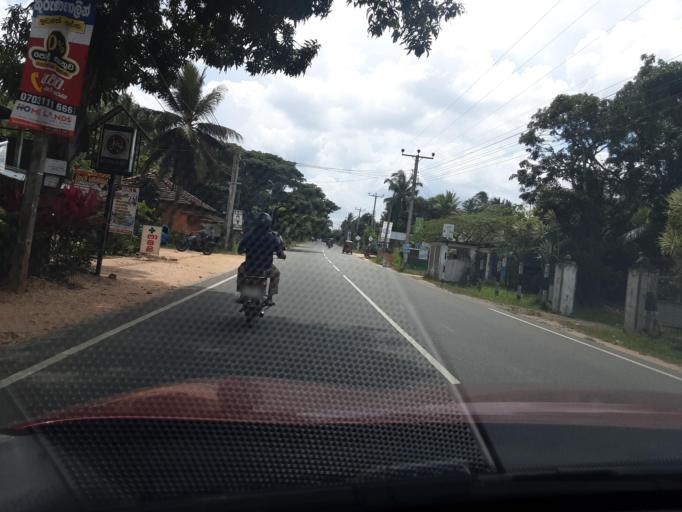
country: LK
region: North Western
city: Kuliyapitiya
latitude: 7.4526
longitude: 80.1814
